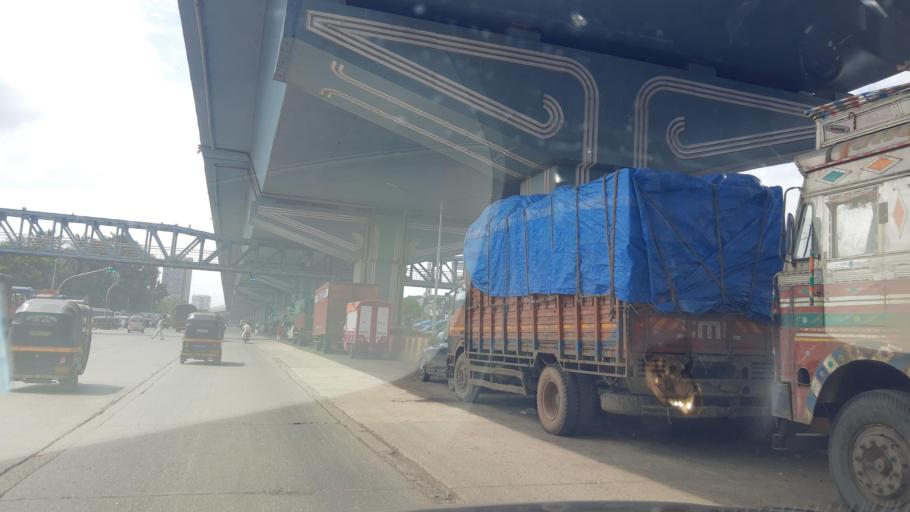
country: IN
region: Maharashtra
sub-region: Mumbai Suburban
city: Mumbai
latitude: 19.0582
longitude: 72.9255
